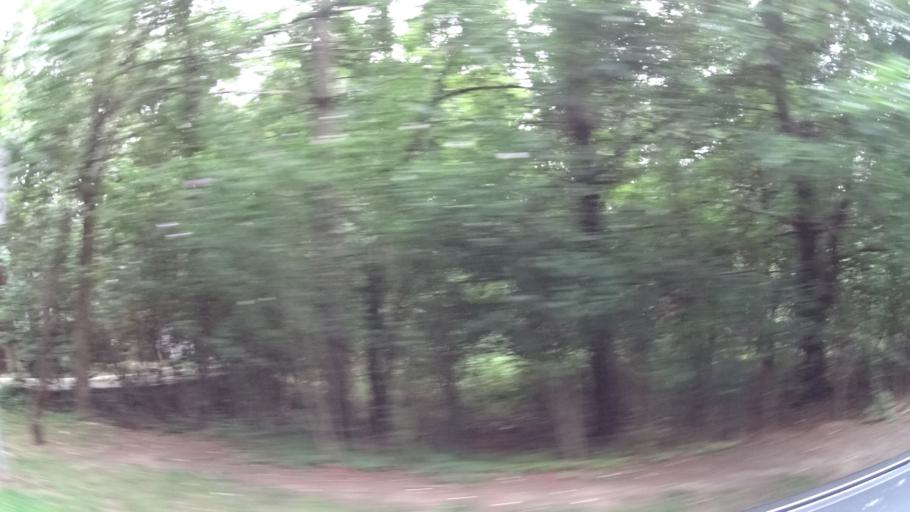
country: US
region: New Jersey
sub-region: Somerset County
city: Warren Township
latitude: 40.6100
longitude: -74.4906
